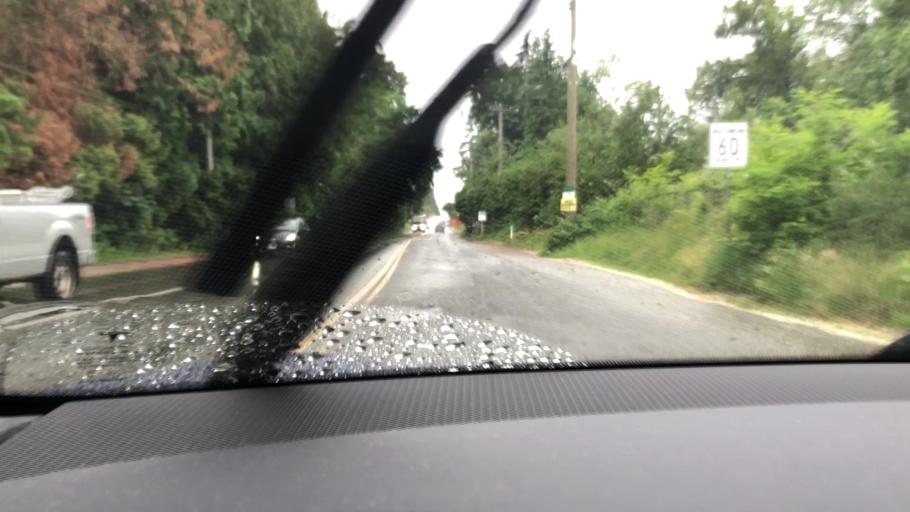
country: CA
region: British Columbia
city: Walnut Grove
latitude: 49.1334
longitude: -122.6465
